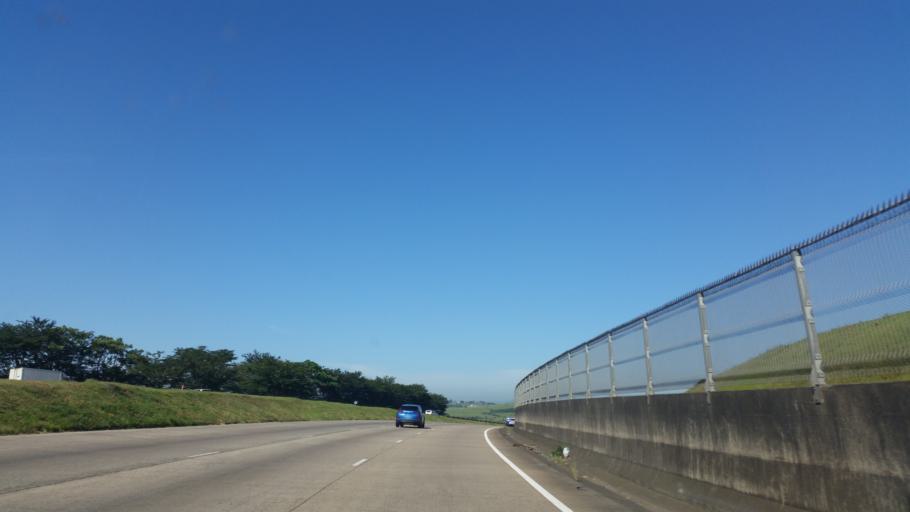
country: ZA
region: KwaZulu-Natal
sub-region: eThekwini Metropolitan Municipality
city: Mpumalanga
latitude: -29.7419
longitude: 30.6321
